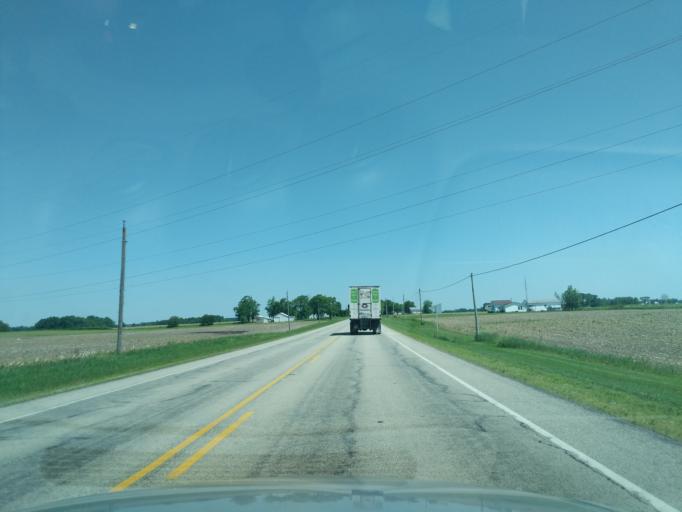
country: US
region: Indiana
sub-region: Whitley County
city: Columbia City
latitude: 41.0645
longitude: -85.4704
